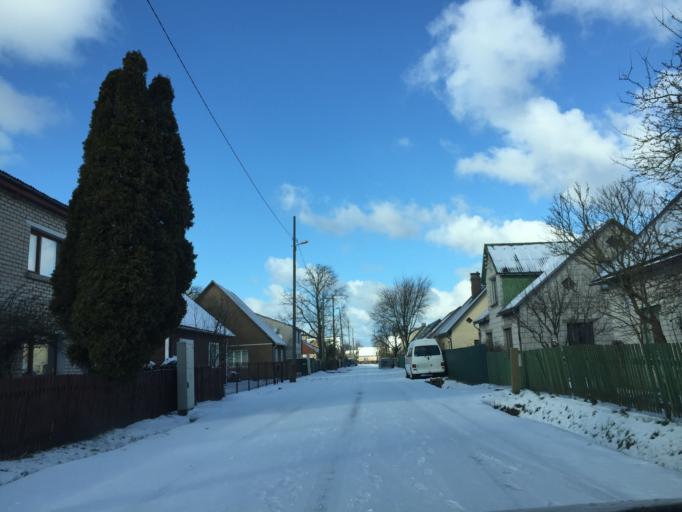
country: LV
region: Ventspils
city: Ventspils
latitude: 57.3791
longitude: 21.5624
